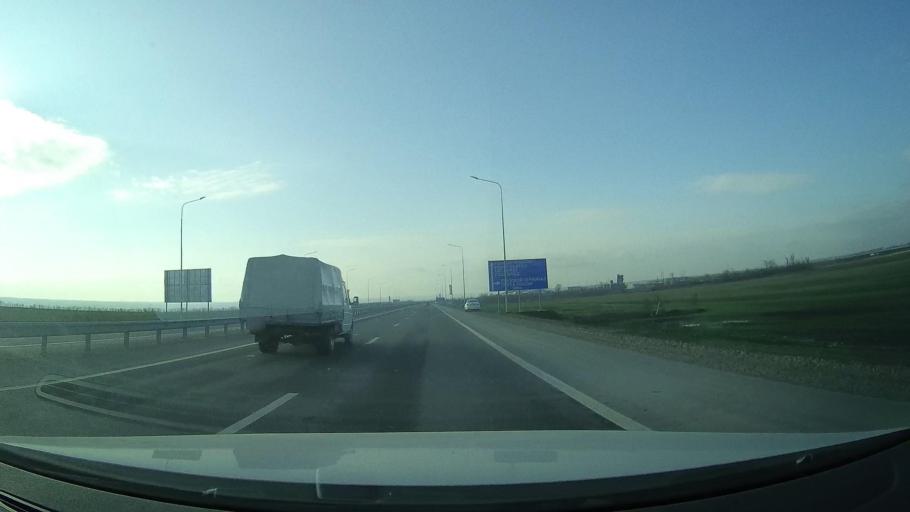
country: RU
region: Rostov
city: Grushevskaya
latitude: 47.4983
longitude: 39.9603
